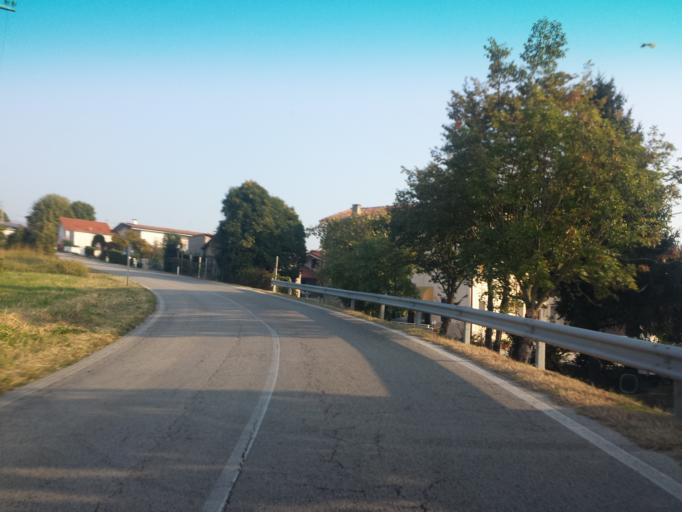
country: IT
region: Veneto
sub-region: Provincia di Vicenza
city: Breganze
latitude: 45.7110
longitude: 11.5758
